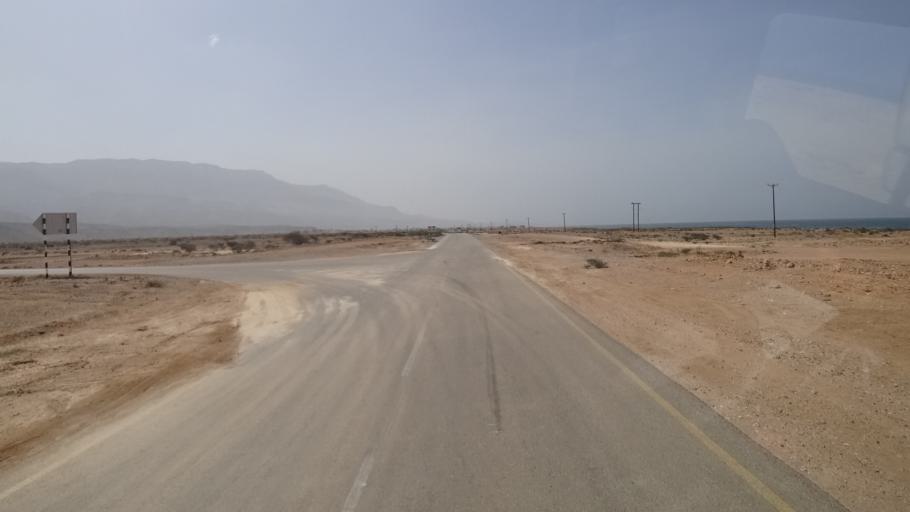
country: OM
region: Ash Sharqiyah
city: Sur
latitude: 22.9805
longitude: 59.1533
